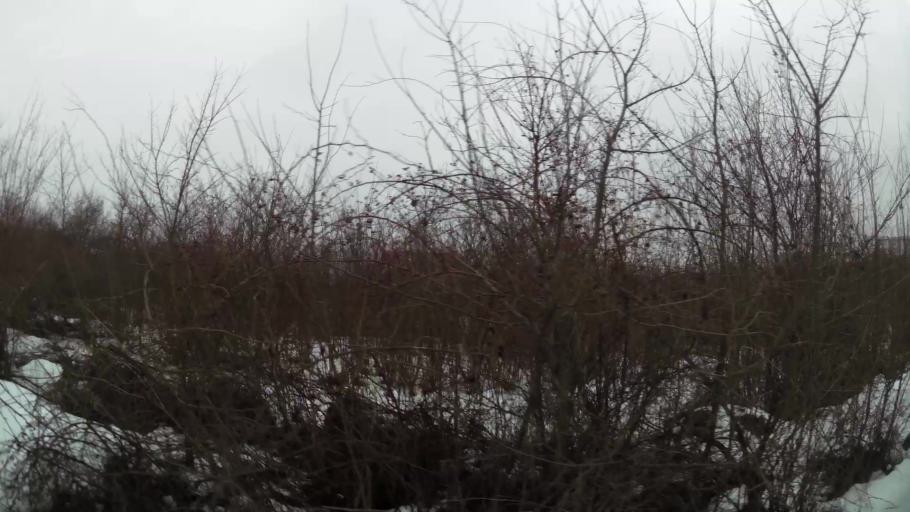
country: RS
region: Central Serbia
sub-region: Belgrade
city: Zvezdara
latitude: 44.7572
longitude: 20.5068
